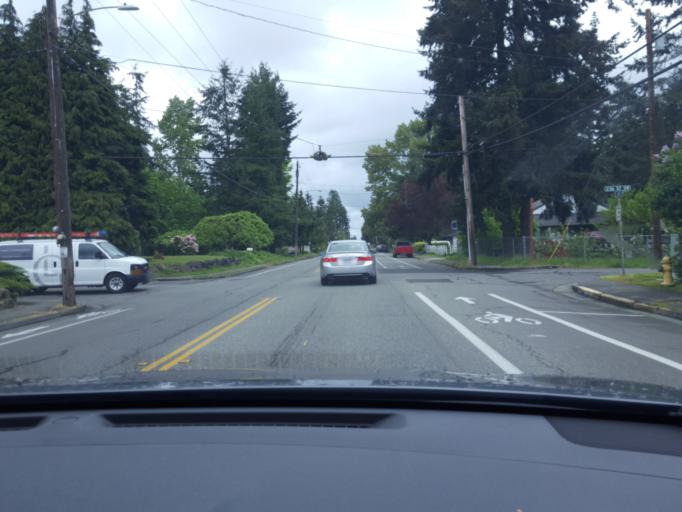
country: US
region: Washington
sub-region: Snohomish County
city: Esperance
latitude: 47.7849
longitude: -122.3354
